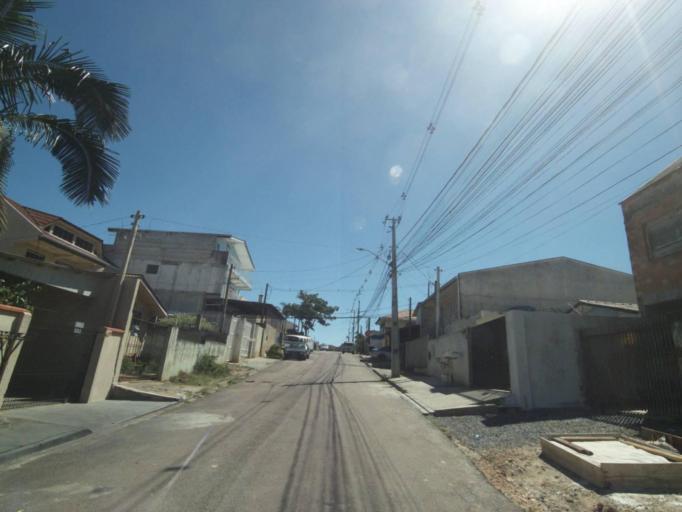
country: BR
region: Parana
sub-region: Curitiba
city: Curitiba
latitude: -25.4624
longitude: -49.3414
